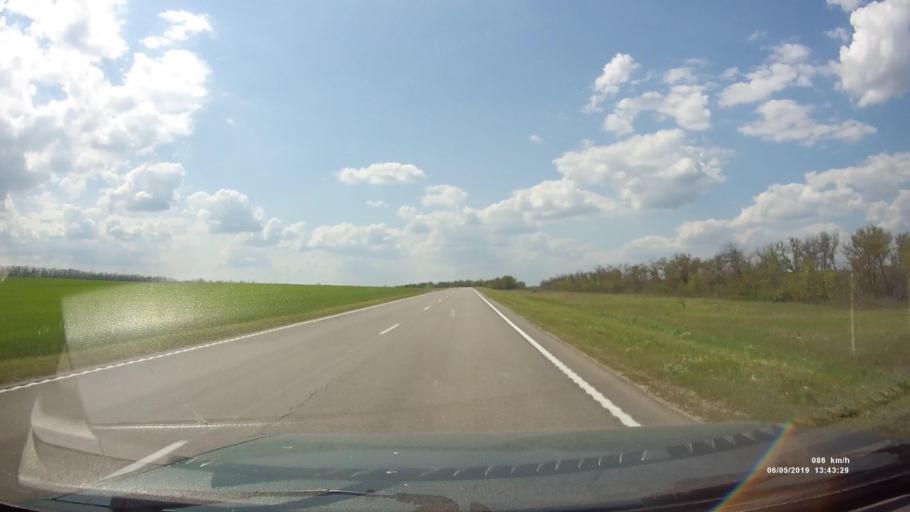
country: RU
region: Rostov
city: Semikarakorsk
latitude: 47.6606
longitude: 40.6376
